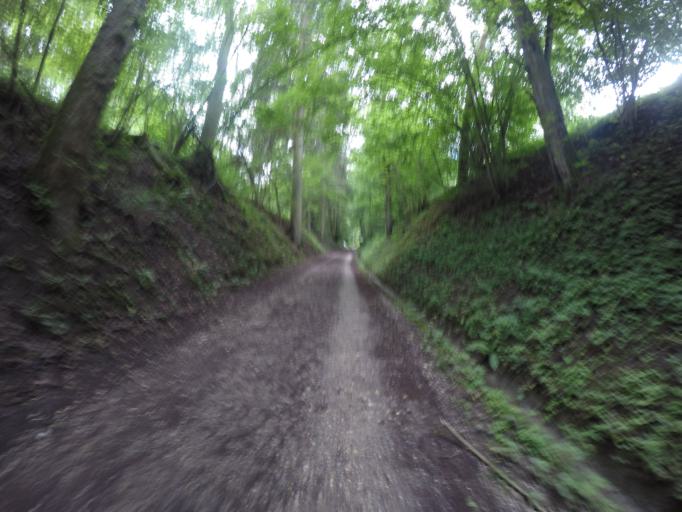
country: DE
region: Bavaria
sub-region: Lower Bavaria
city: Landshut
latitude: 48.5189
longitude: 12.1388
